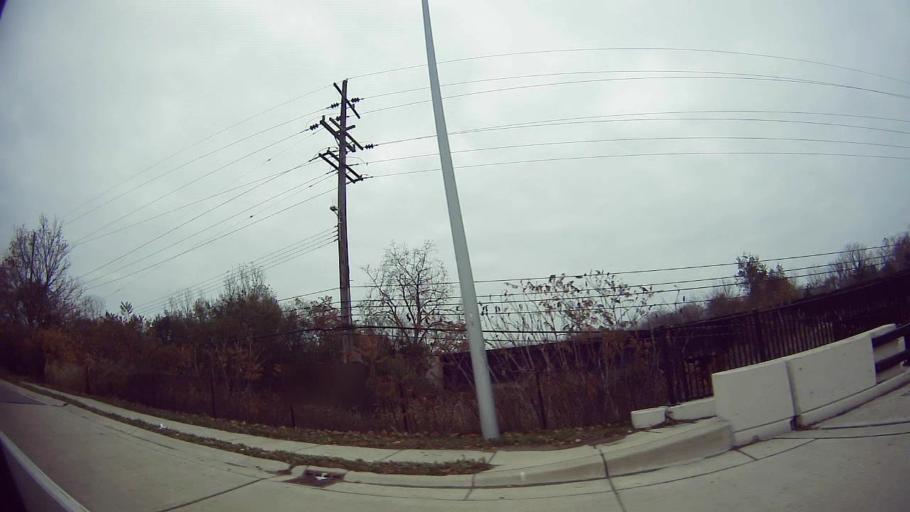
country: US
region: Michigan
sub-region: Wayne County
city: Dearborn
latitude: 42.3091
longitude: -83.2214
